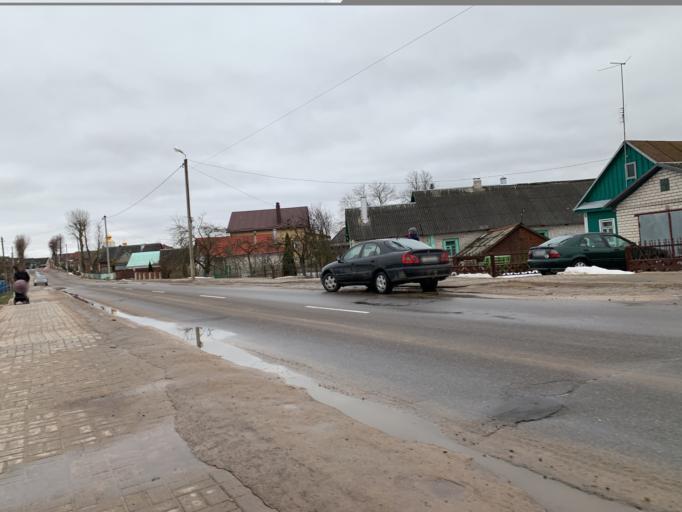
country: BY
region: Minsk
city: Nyasvizh
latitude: 53.2271
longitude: 26.6780
